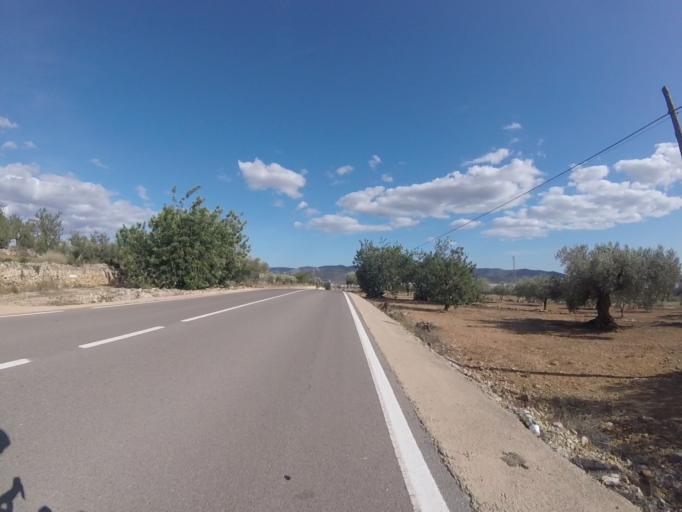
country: ES
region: Valencia
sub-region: Provincia de Castello
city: Alcala de Xivert
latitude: 40.3022
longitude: 0.1946
